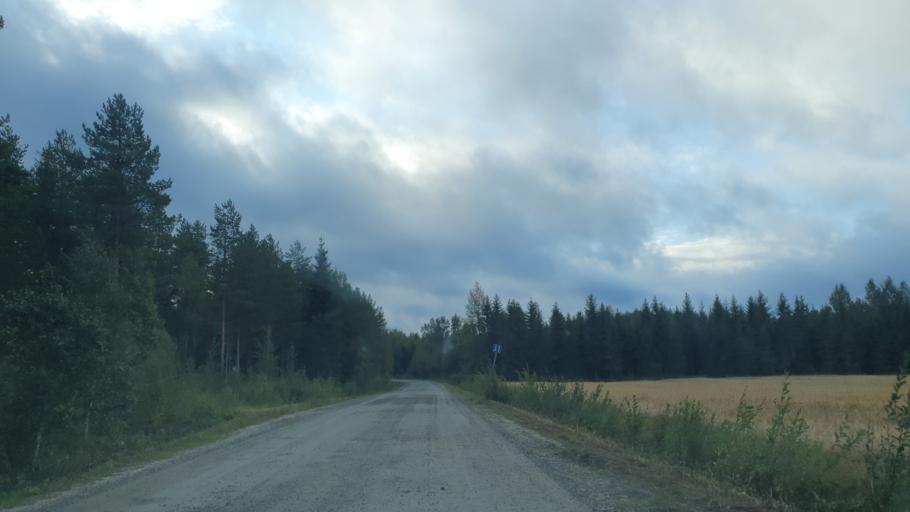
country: FI
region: Kainuu
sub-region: Kehys-Kainuu
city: Kuhmo
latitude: 64.1331
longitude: 29.5832
